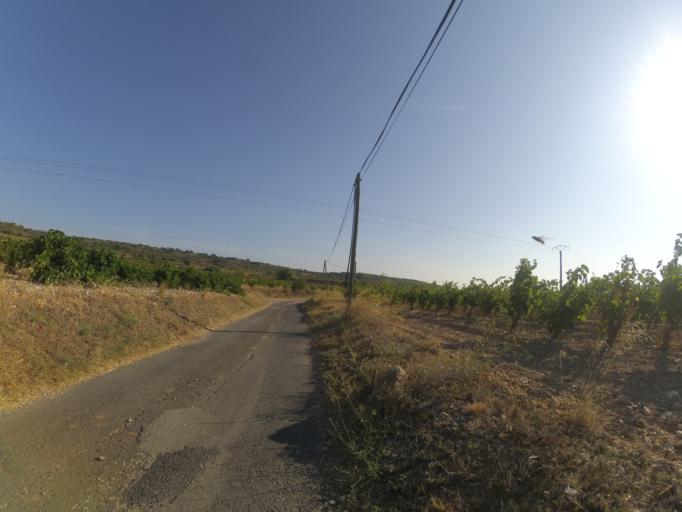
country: FR
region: Languedoc-Roussillon
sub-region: Departement des Pyrenees-Orientales
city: Baixas
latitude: 42.7471
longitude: 2.7922
